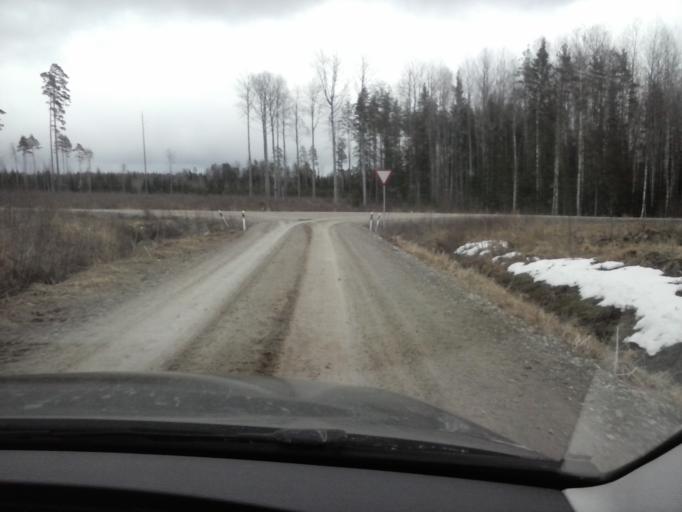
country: EE
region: Jogevamaa
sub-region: Mustvee linn
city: Mustvee
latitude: 59.0607
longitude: 26.8648
